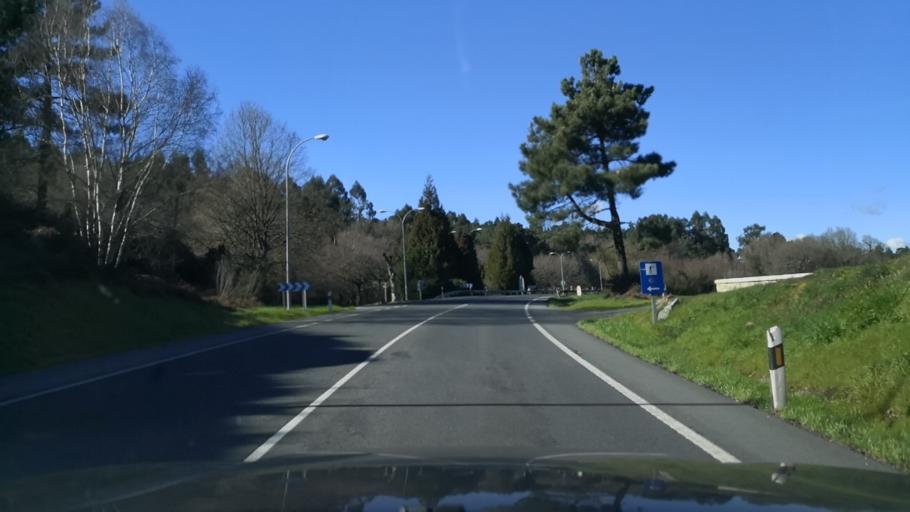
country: ES
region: Galicia
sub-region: Provincia de Pontevedra
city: Silleda
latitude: 42.6866
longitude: -8.2186
